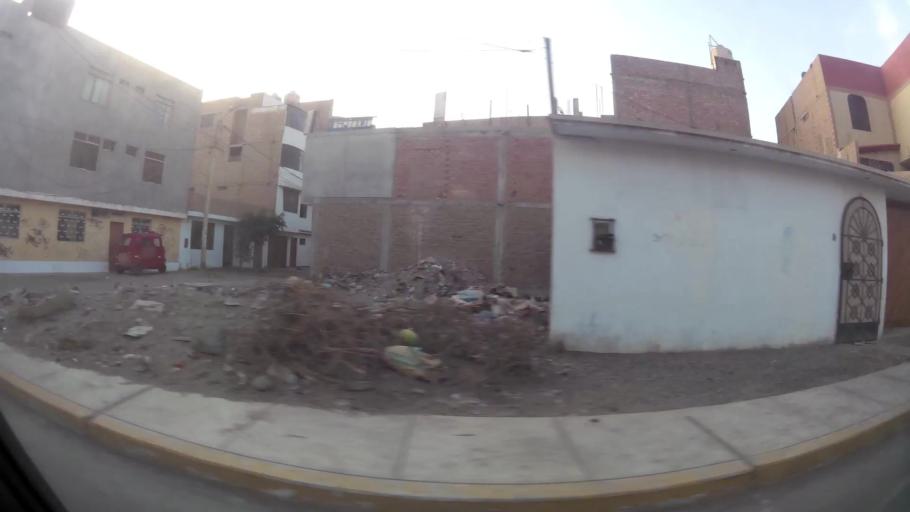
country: PE
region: Lima
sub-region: Huaura
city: Huacho
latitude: -11.1177
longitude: -77.6085
